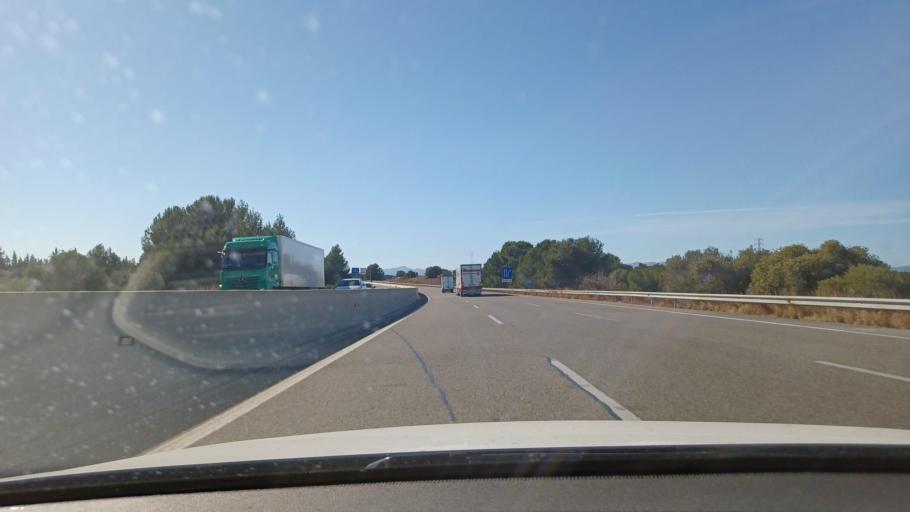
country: ES
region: Catalonia
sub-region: Provincia de Tarragona
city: Vila-seca
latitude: 41.1162
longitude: 1.1392
